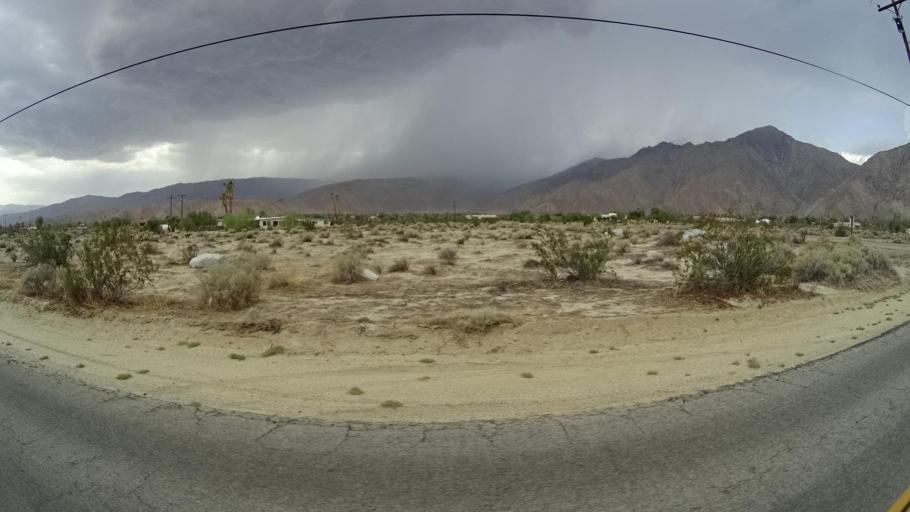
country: US
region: California
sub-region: San Diego County
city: Borrego Springs
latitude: 33.2720
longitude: -116.3861
